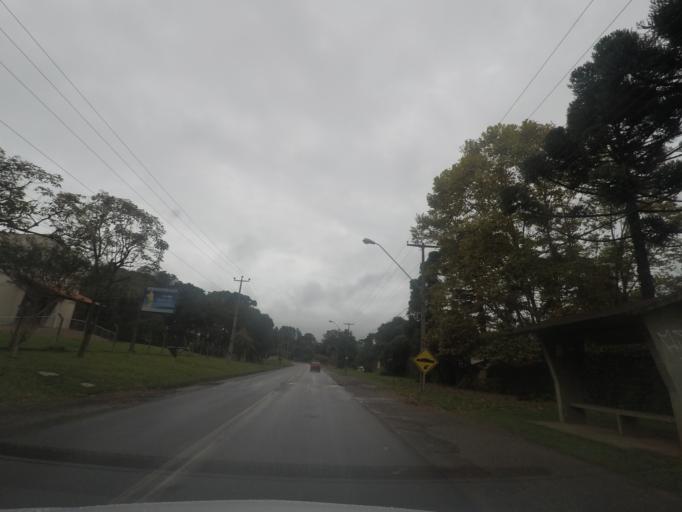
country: BR
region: Parana
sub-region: Campina Grande Do Sul
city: Campina Grande do Sul
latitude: -25.3228
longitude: -49.0778
